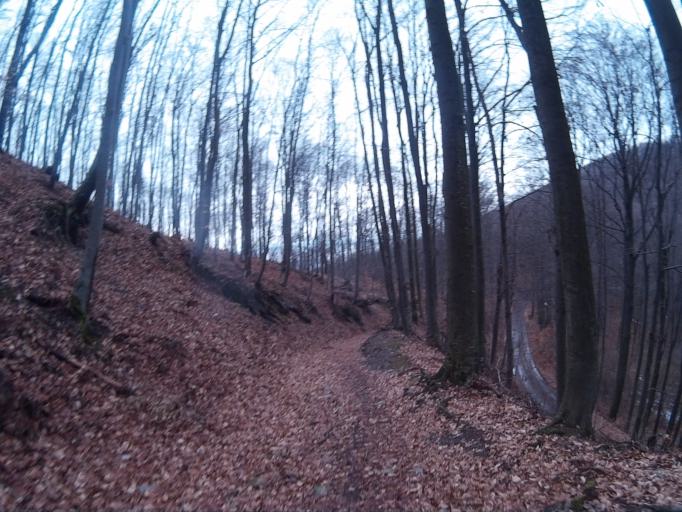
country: HU
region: Heves
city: Belapatfalva
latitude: 48.0581
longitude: 20.4005
